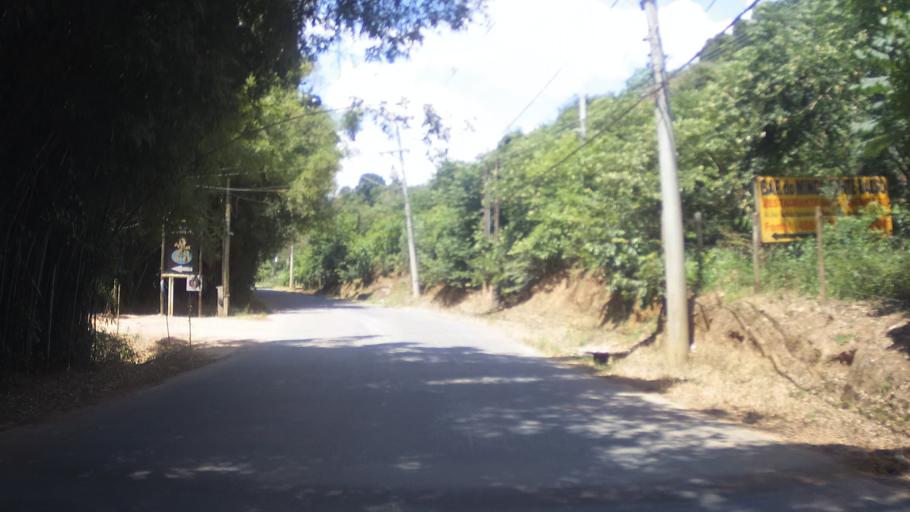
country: BR
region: Sao Paulo
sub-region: Campo Limpo Paulista
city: Campo Limpo Paulista
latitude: -23.1283
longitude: -46.8085
